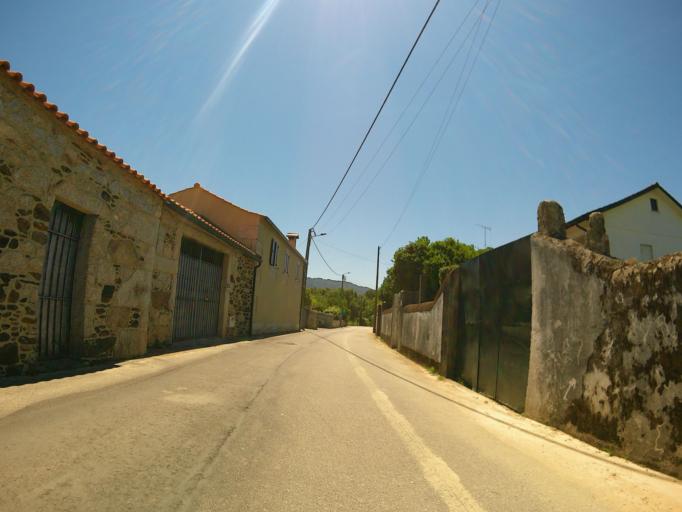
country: PT
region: Viana do Castelo
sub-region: Viana do Castelo
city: Darque
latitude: 41.7138
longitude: -8.7153
